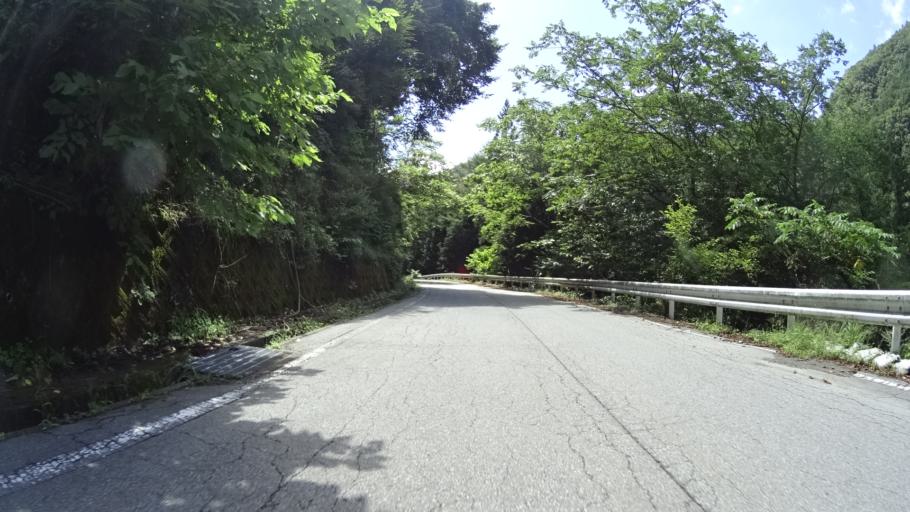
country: JP
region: Yamanashi
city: Enzan
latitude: 35.6646
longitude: 138.8075
